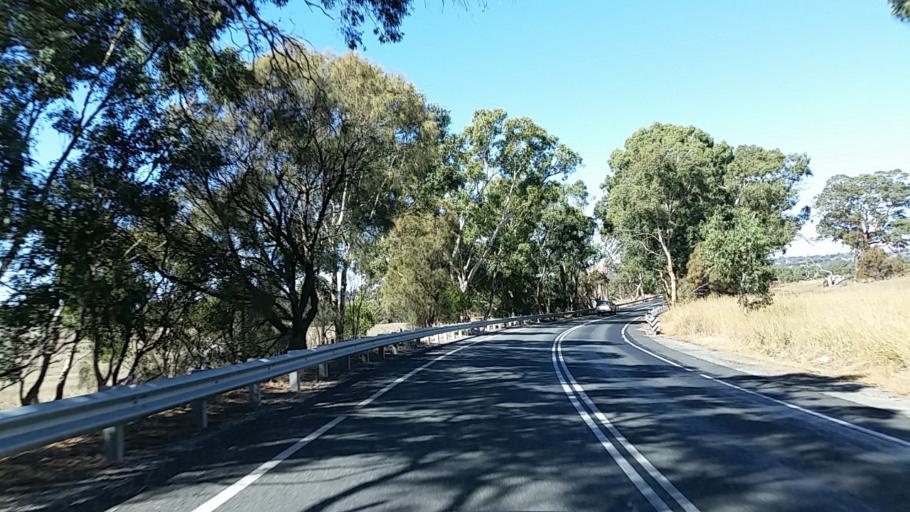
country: AU
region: South Australia
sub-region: Adelaide Hills
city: Birdwood
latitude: -34.7619
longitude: 139.0128
